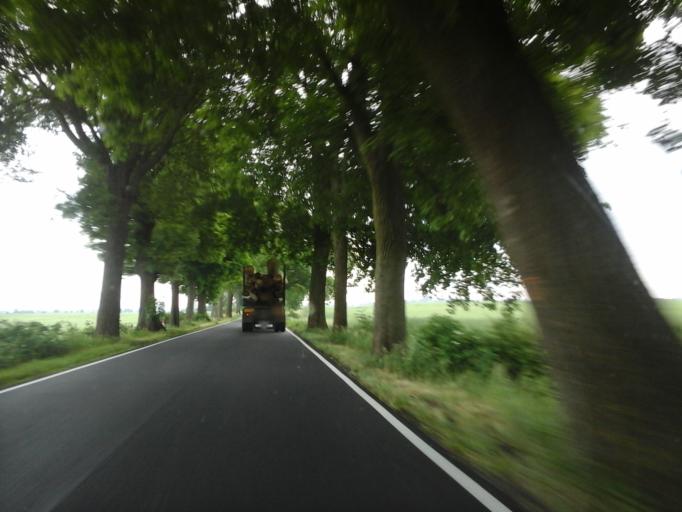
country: PL
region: West Pomeranian Voivodeship
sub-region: Powiat choszczenski
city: Recz
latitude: 53.1858
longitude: 15.5590
